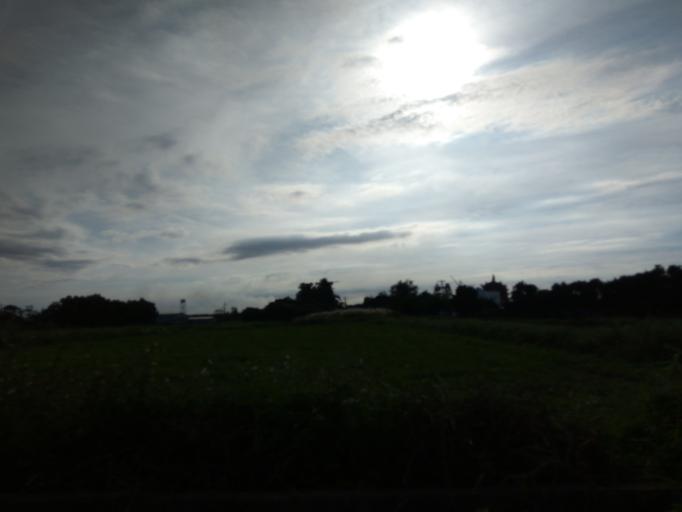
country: TW
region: Taiwan
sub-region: Hsinchu
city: Zhubei
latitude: 24.9420
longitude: 120.9913
